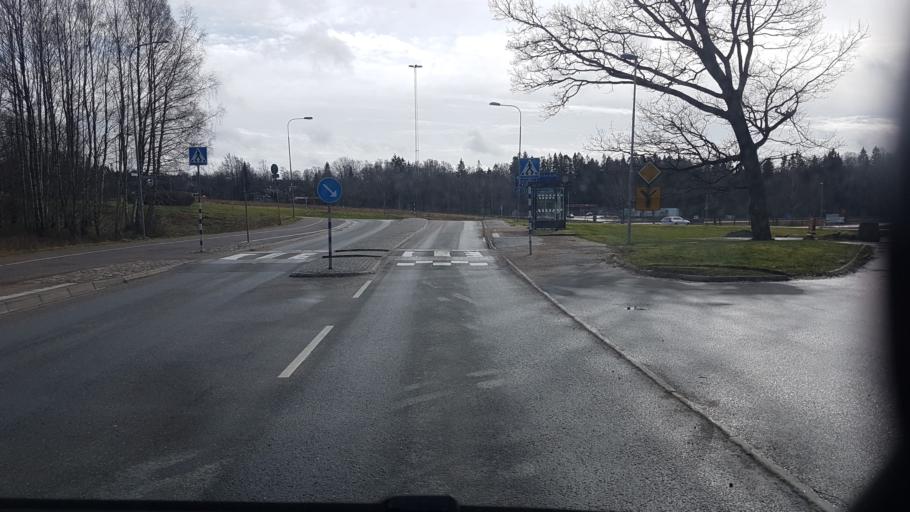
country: SE
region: Vaestra Goetaland
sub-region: Lerums Kommun
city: Stenkullen
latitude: 57.8037
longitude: 12.3651
